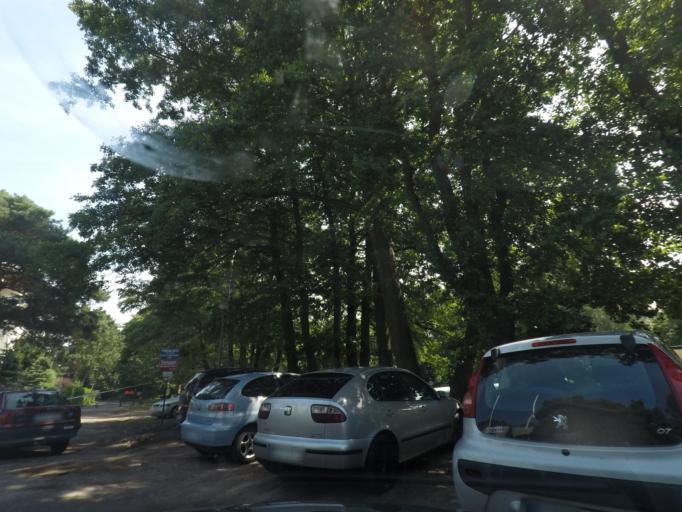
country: PL
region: Pomeranian Voivodeship
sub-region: Powiat slupski
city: Ustka
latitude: 54.5829
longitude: 16.8682
